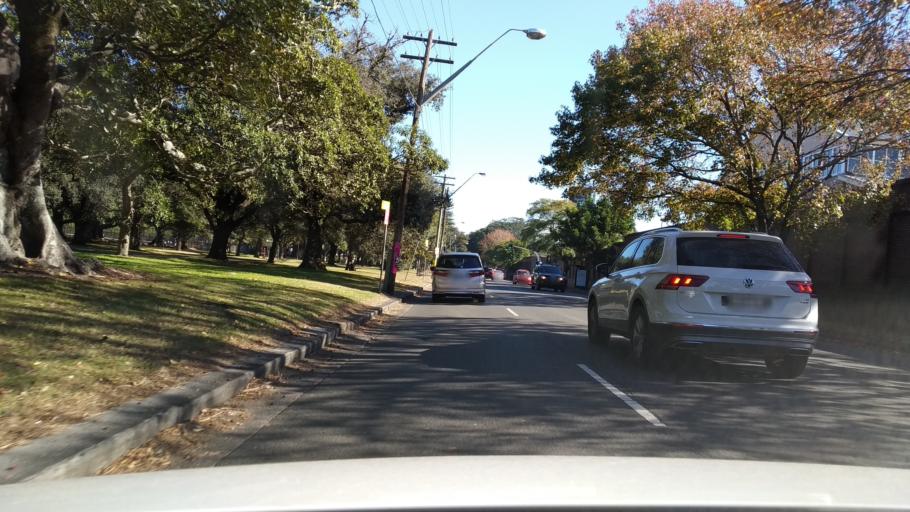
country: AU
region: New South Wales
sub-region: Woollahra
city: Paddington
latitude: -33.8966
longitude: 151.2262
